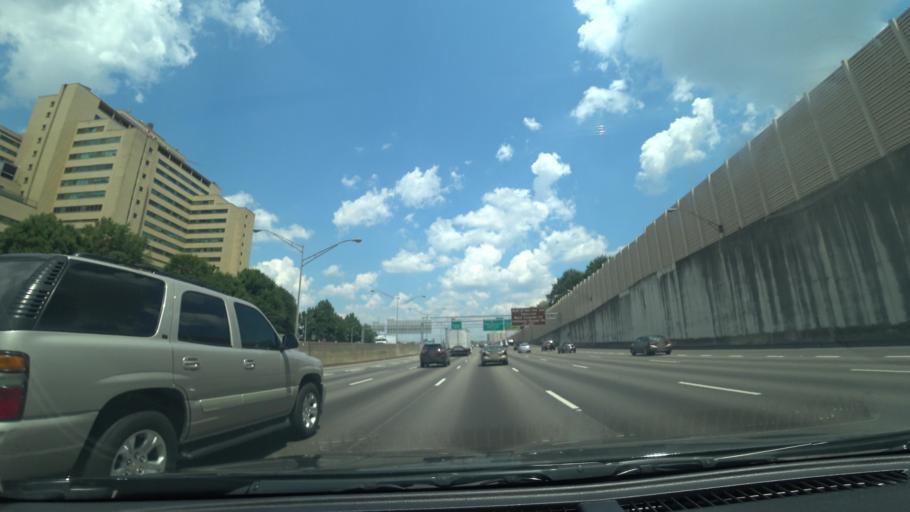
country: US
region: Georgia
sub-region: Fulton County
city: Atlanta
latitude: 33.7516
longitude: -84.3818
